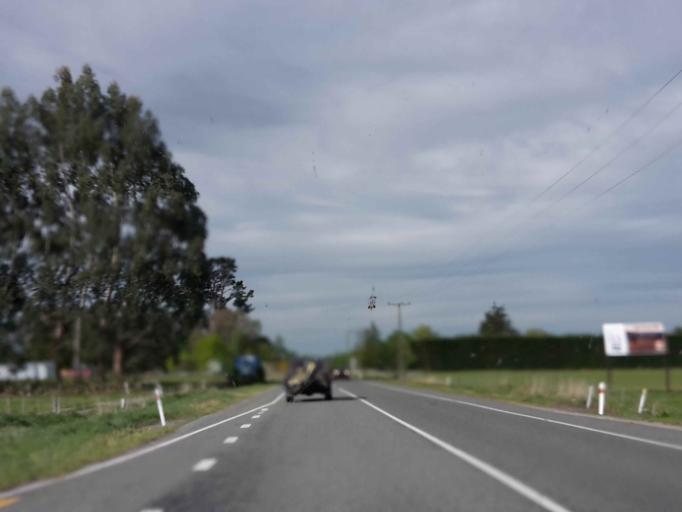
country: NZ
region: Canterbury
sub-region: Timaru District
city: Pleasant Point
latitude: -44.1090
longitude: 171.2327
